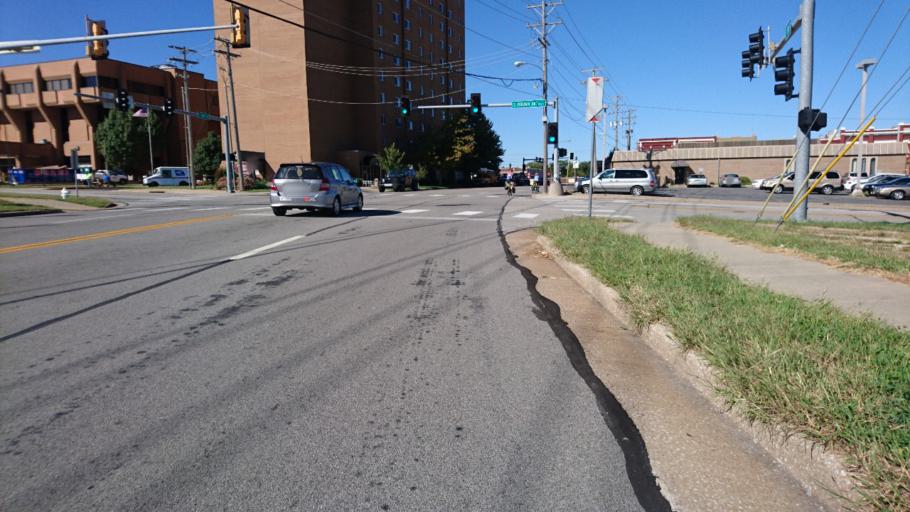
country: US
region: Missouri
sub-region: Jasper County
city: Joplin
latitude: 37.0898
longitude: -94.5118
